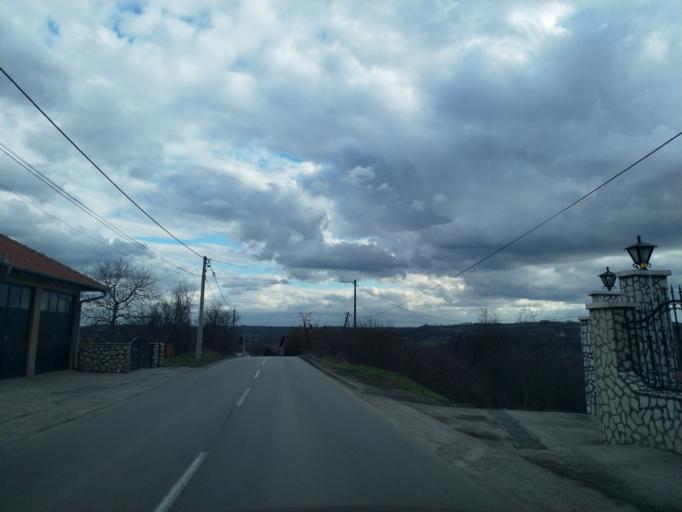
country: RS
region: Central Serbia
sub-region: Belgrade
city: Grocka
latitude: 44.5868
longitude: 20.7318
